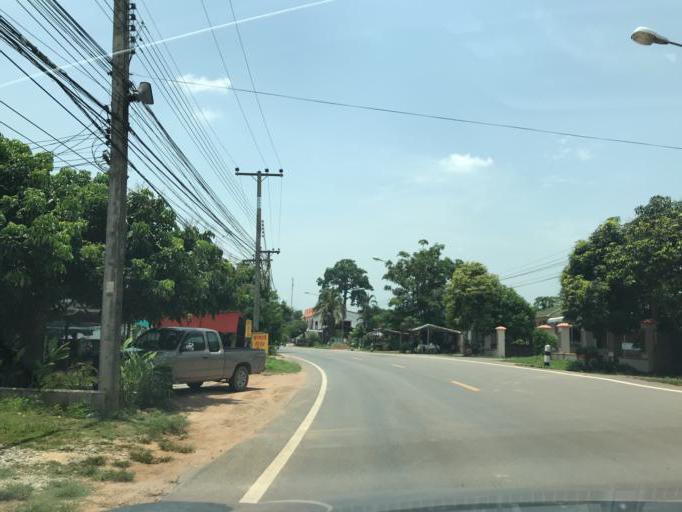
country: TH
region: Lamphun
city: Thung Hua Chang
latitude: 18.0012
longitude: 99.0296
